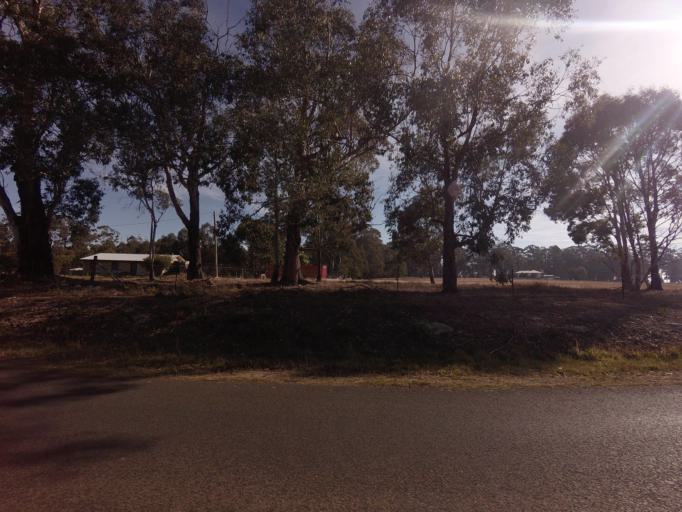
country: AU
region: Tasmania
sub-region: Sorell
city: Sorell
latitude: -42.4642
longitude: 147.4613
